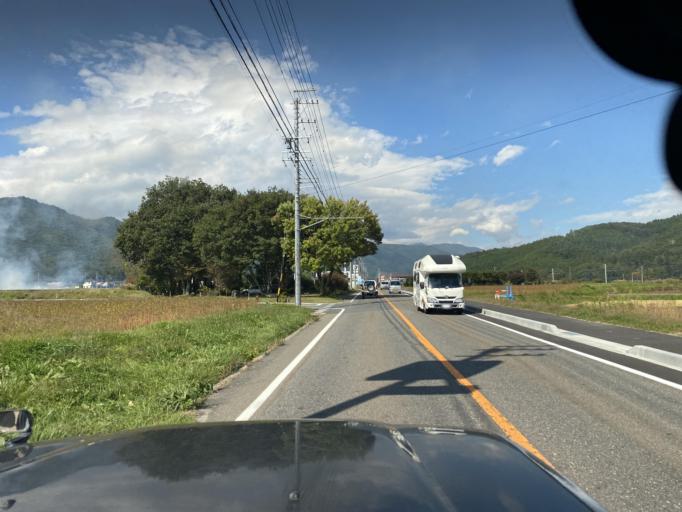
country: JP
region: Nagano
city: Omachi
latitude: 36.5305
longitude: 137.8480
